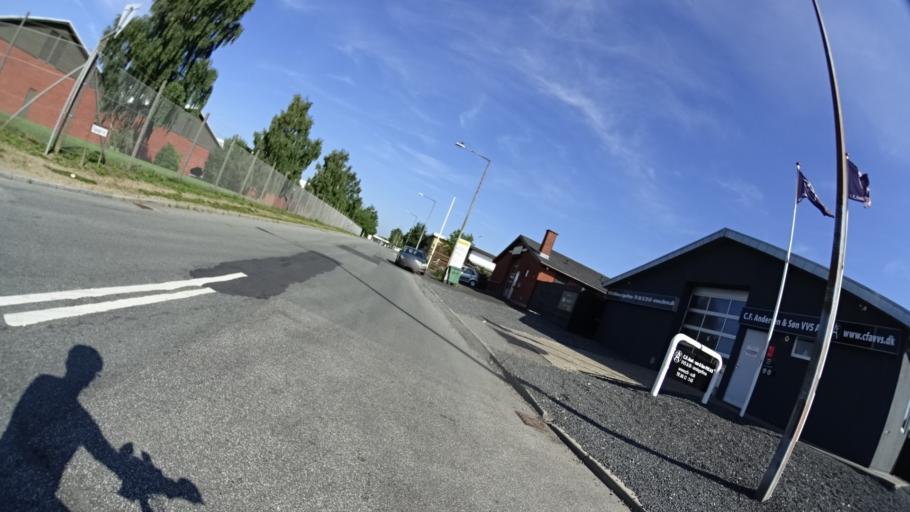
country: DK
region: Central Jutland
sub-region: Arhus Kommune
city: Stavtrup
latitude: 56.1427
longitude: 10.1478
